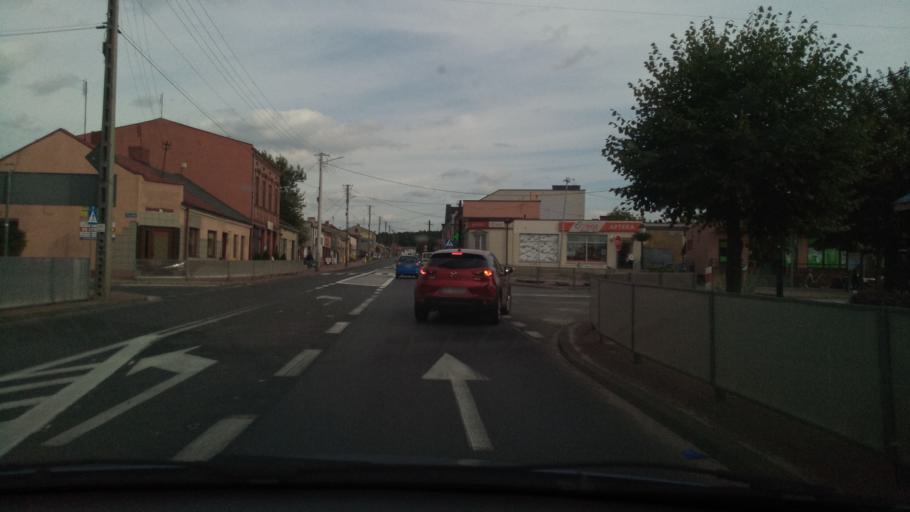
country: PL
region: Lodz Voivodeship
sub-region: Powiat piotrkowski
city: Sulejow
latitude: 51.3541
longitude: 19.8864
